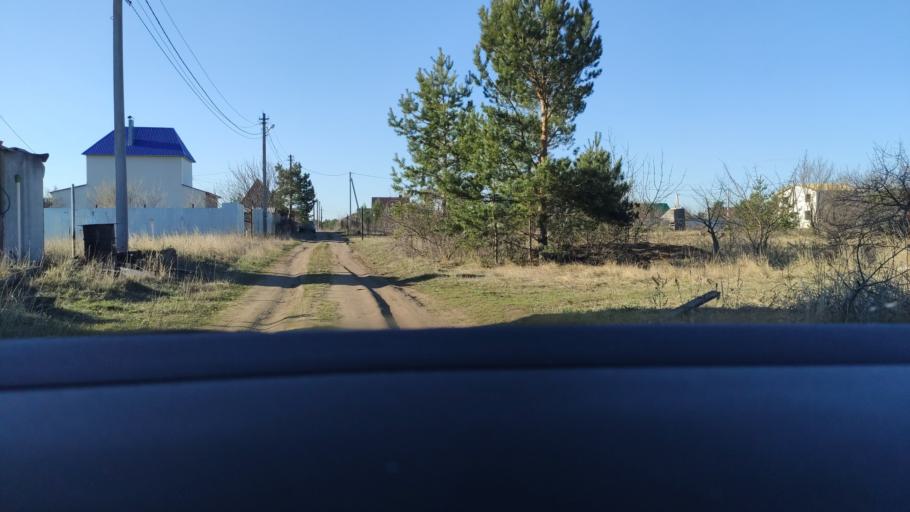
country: RU
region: Voronezj
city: Pridonskoy
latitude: 51.6351
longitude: 39.1132
